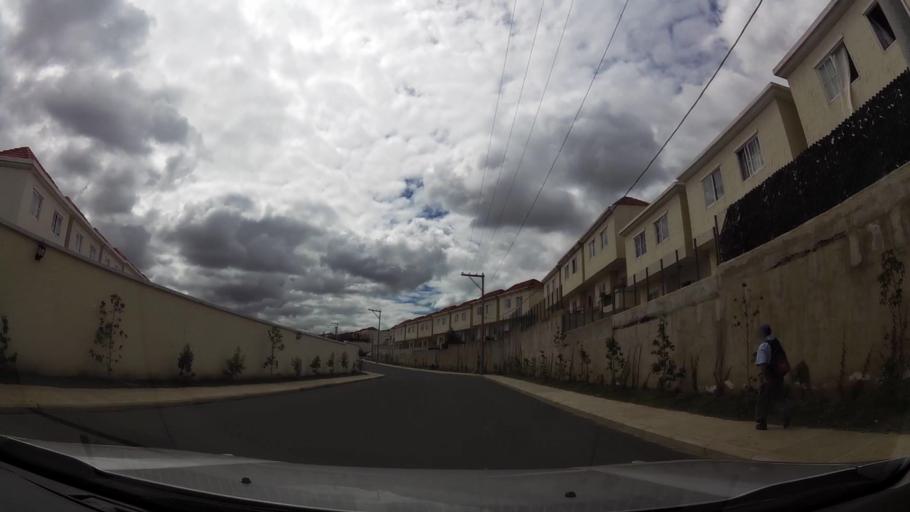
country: GT
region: Guatemala
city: Guatemala City
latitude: 14.6737
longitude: -90.5585
